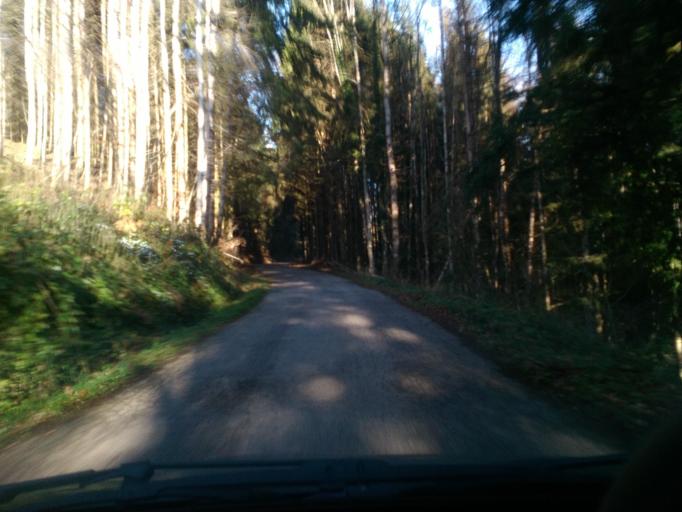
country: FR
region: Lorraine
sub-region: Departement des Vosges
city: Senones
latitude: 48.3468
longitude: 6.9719
